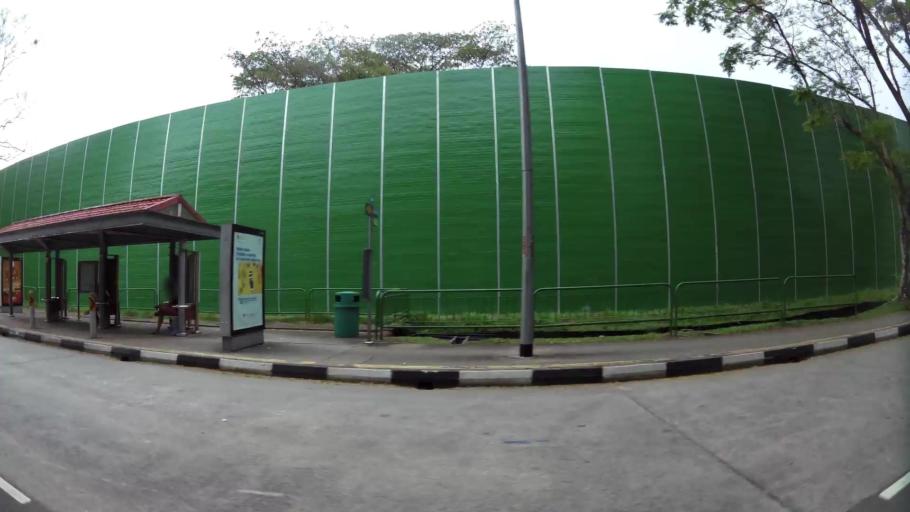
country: SG
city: Singapore
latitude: 1.3824
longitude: 103.8359
